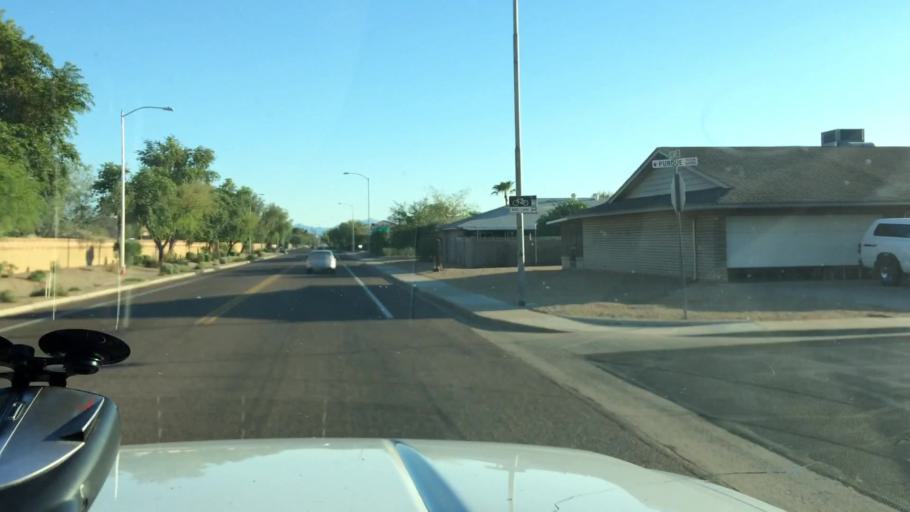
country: US
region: Arizona
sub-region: Maricopa County
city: Sun City
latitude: 33.5724
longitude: -112.2639
